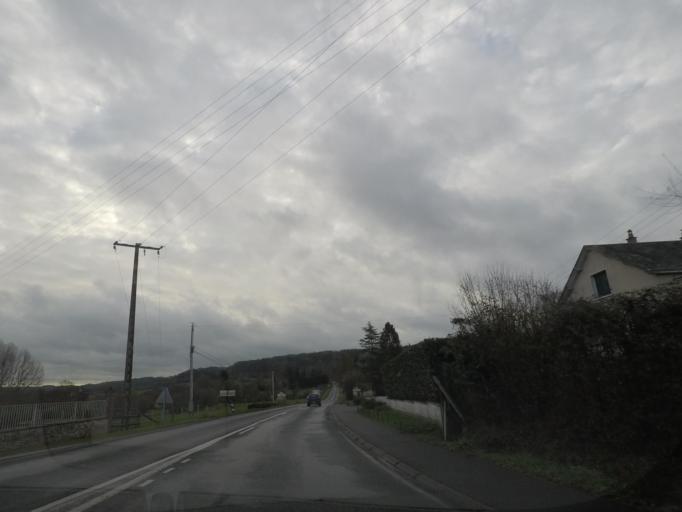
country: FR
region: Pays de la Loire
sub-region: Departement de la Sarthe
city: Vibraye
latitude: 48.0522
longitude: 0.7377
